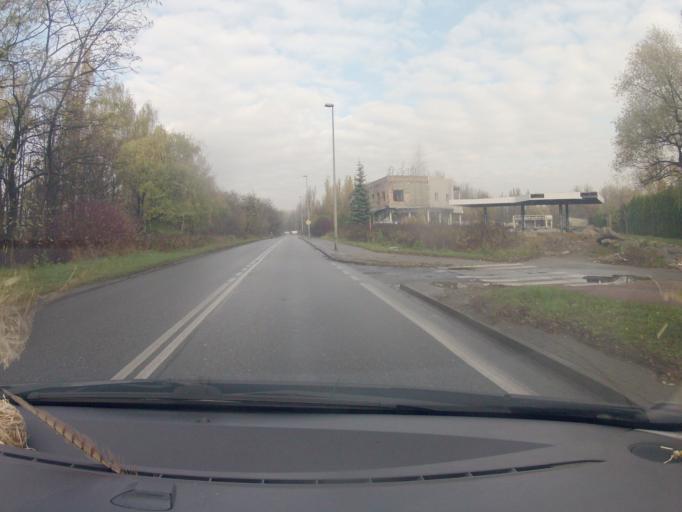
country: PL
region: Lesser Poland Voivodeship
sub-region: Powiat wielicki
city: Kokotow
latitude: 50.0752
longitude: 20.0628
